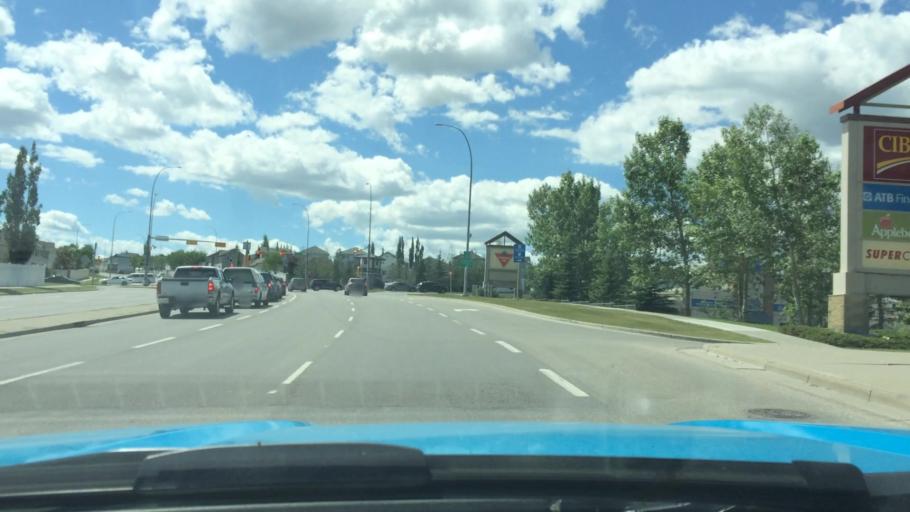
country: CA
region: Alberta
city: Calgary
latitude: 51.1540
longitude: -114.0650
